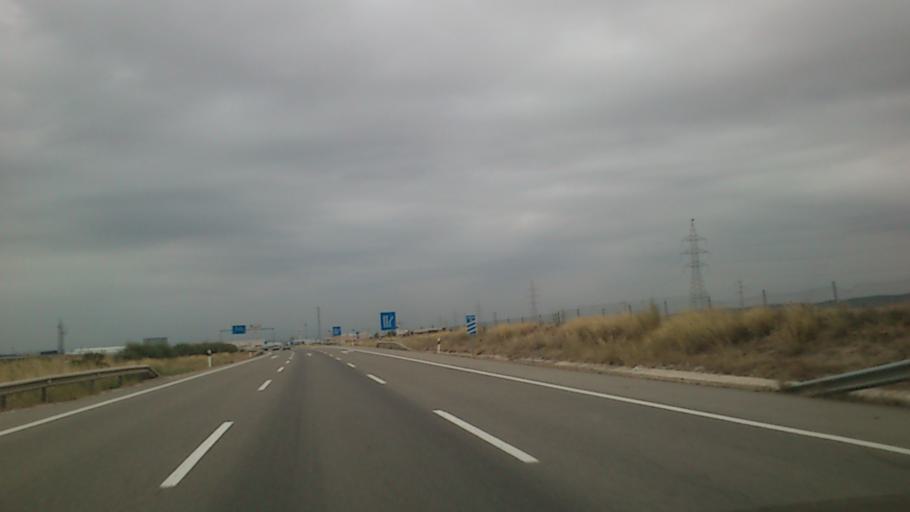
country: ES
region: Aragon
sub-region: Provincia de Zaragoza
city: Villanueva de Gallego
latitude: 41.7696
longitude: -0.8353
